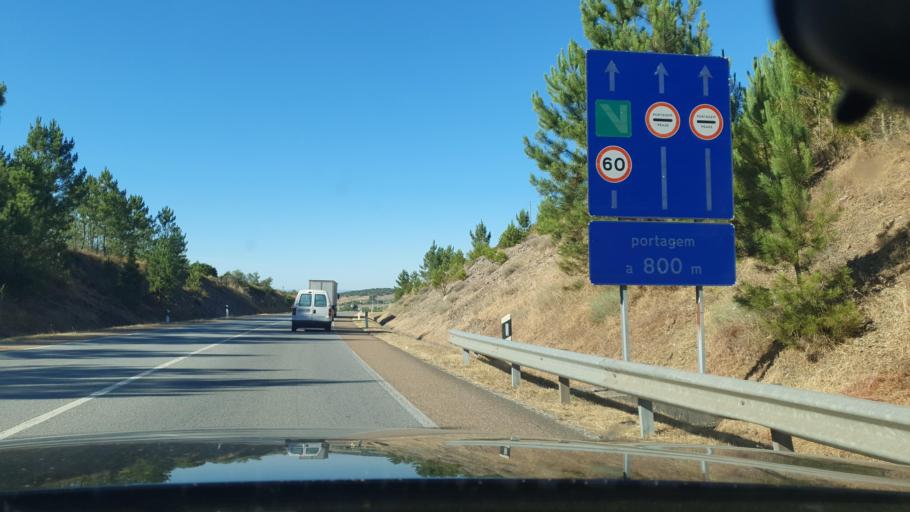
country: PT
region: Evora
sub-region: Borba
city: Borba
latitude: 38.8091
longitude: -7.4776
